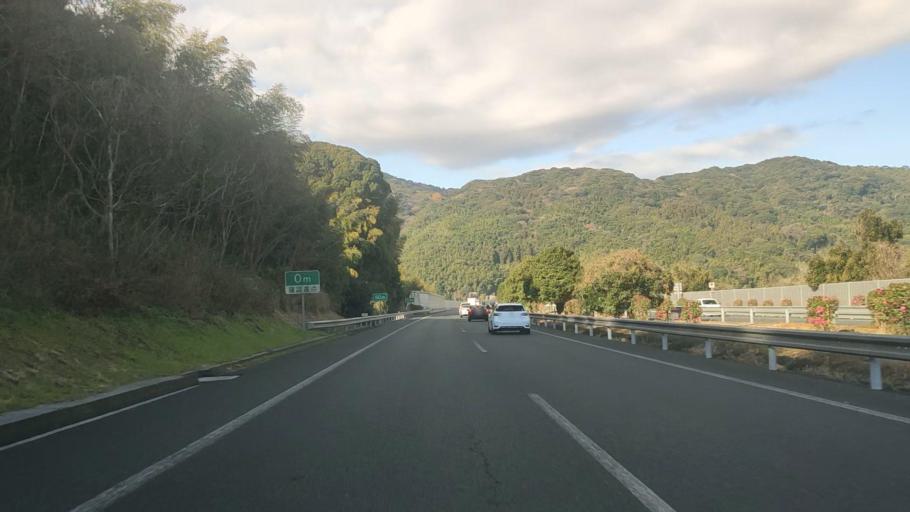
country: JP
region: Fukuoka
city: Kanda
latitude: 33.8040
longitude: 130.9282
